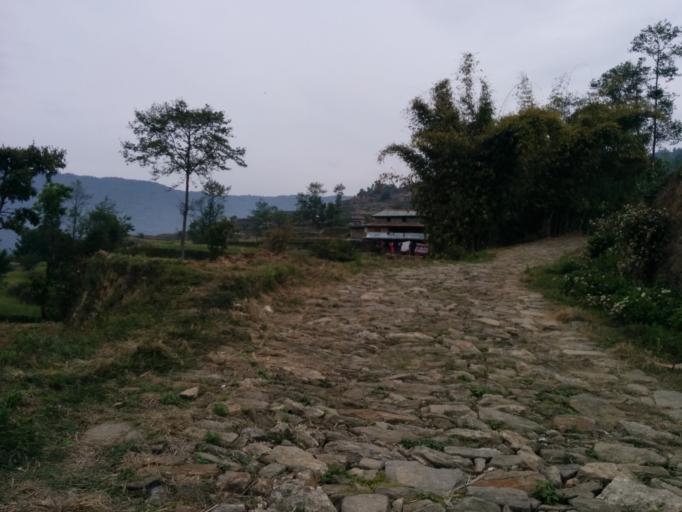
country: NP
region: Central Region
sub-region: Bagmati Zone
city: Bhaktapur
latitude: 27.7757
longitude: 85.4296
